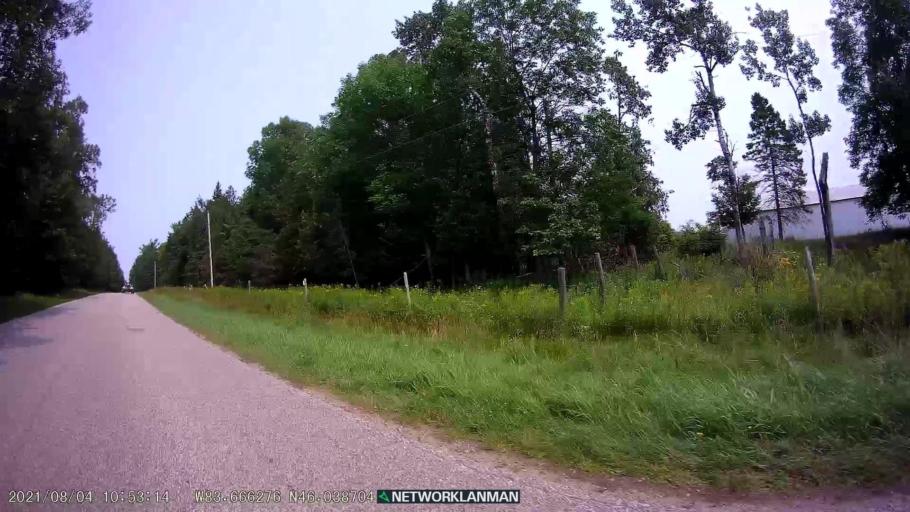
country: CA
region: Ontario
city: Thessalon
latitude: 46.0398
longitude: -83.6663
